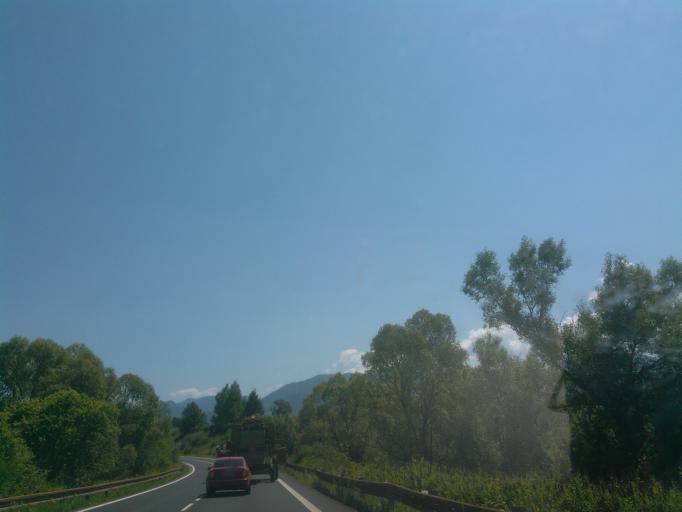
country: SK
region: Zilinsky
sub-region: Okres Liptovsky Mikulas
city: Liptovsky Mikulas
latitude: 49.0566
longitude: 19.4934
